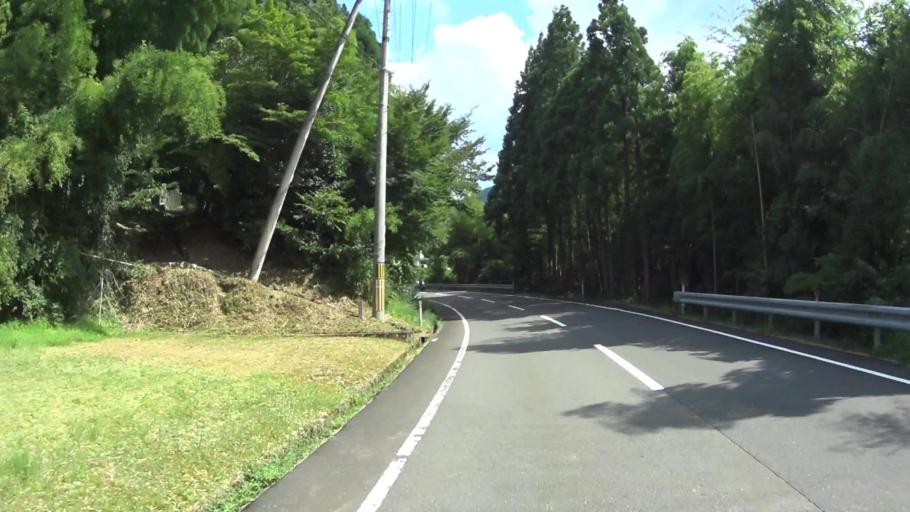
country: JP
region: Fukui
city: Obama
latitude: 35.2744
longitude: 135.5908
